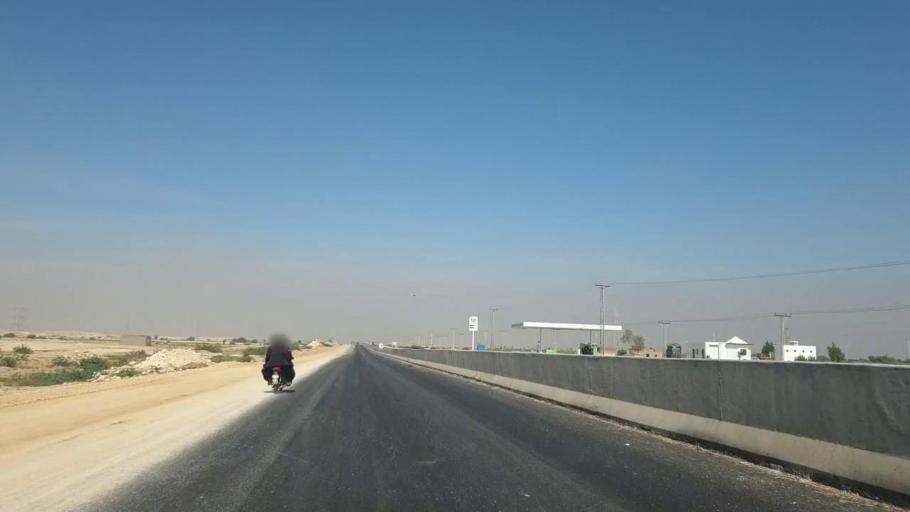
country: PK
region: Sindh
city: Jamshoro
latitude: 25.5124
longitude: 68.2736
